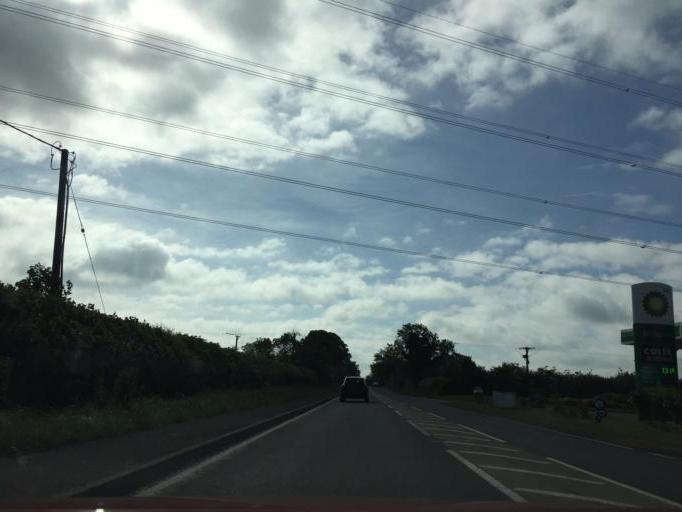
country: GB
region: England
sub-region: Northamptonshire
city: Towcester
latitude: 52.1051
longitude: -0.9397
